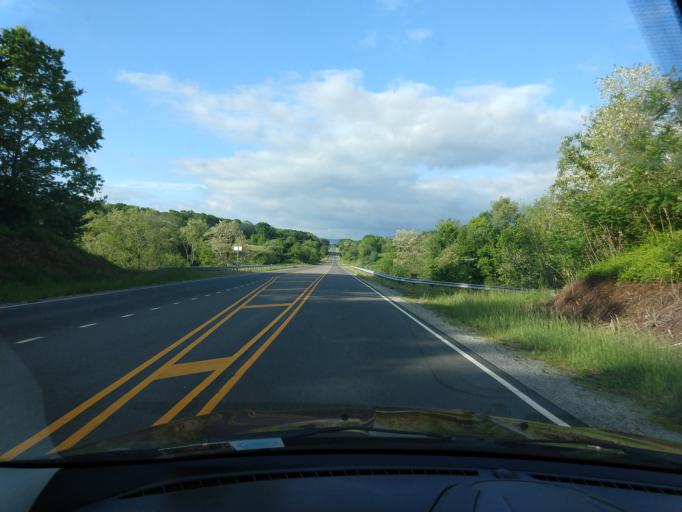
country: US
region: Virginia
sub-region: Wythe County
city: Wytheville
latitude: 36.8923
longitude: -80.9753
